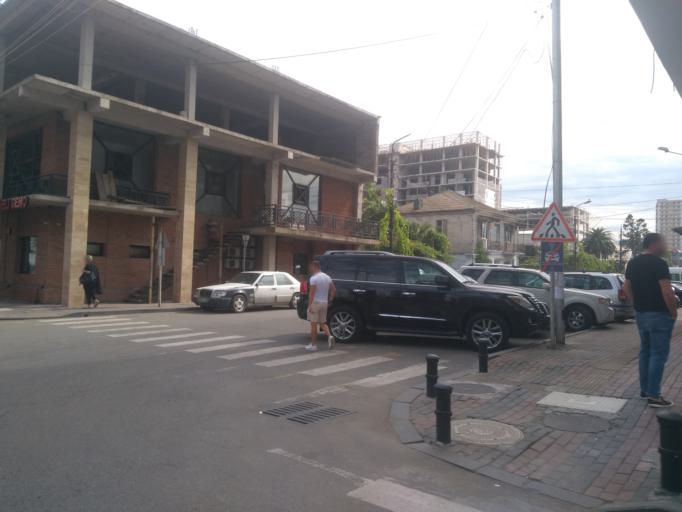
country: GE
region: Ajaria
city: Batumi
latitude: 41.6403
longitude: 41.6291
